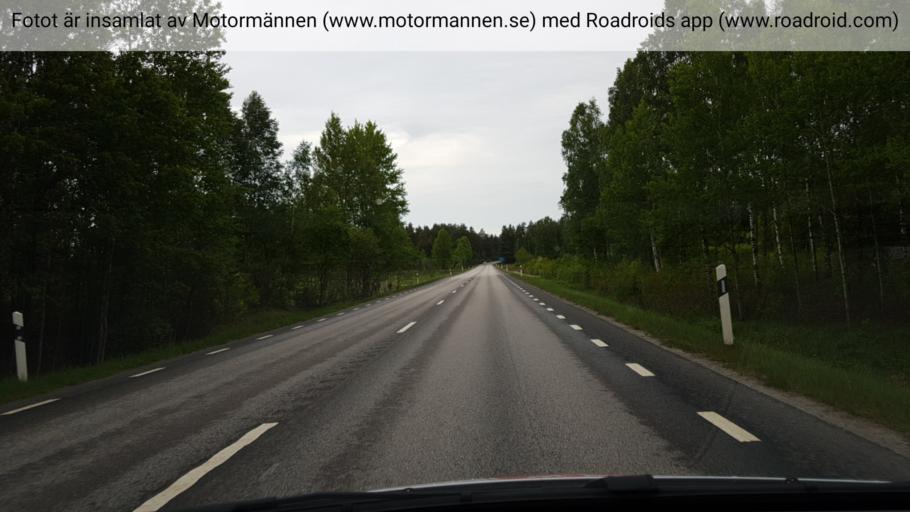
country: SE
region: Kalmar
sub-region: Hultsfreds Kommun
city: Hultsfred
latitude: 57.5740
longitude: 15.8452
